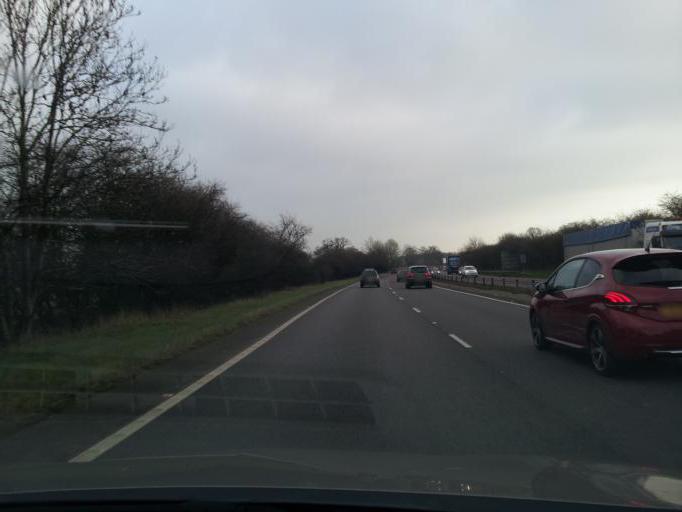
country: GB
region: England
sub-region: Derbyshire
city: Rodsley
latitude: 52.8906
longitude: -1.7656
